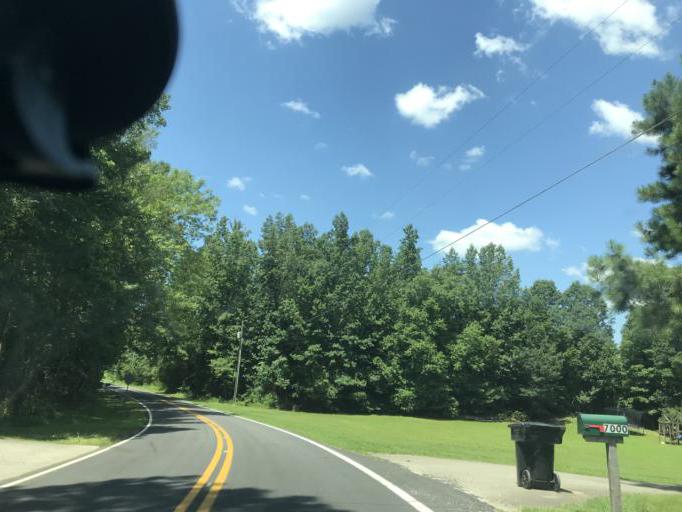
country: US
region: Georgia
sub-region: Forsyth County
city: Cumming
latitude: 34.2689
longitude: -84.2497
